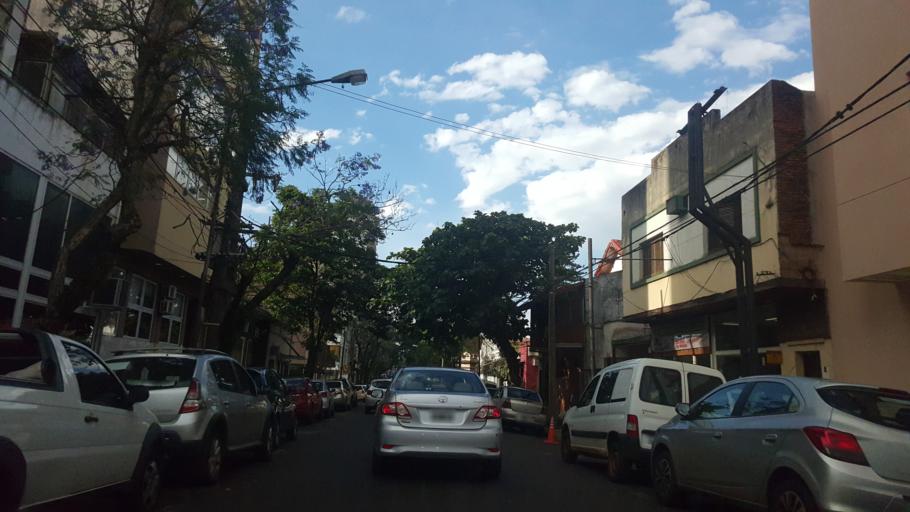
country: AR
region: Misiones
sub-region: Departamento de Capital
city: Posadas
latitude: -27.3725
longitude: -55.8954
